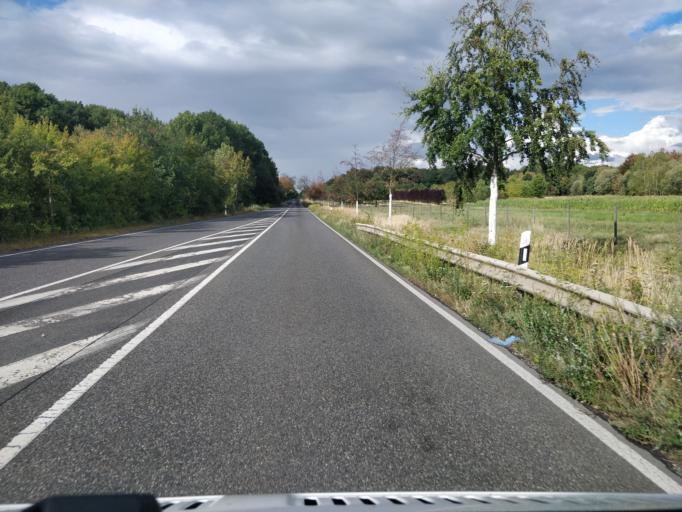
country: DE
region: North Rhine-Westphalia
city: Meckenheim
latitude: 50.6430
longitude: 7.0389
